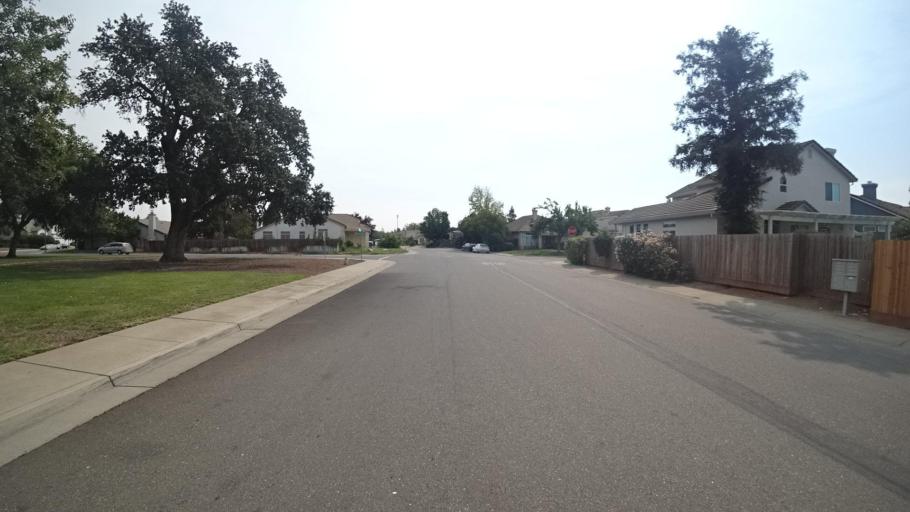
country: US
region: California
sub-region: Sacramento County
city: Laguna
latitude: 38.4152
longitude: -121.4031
